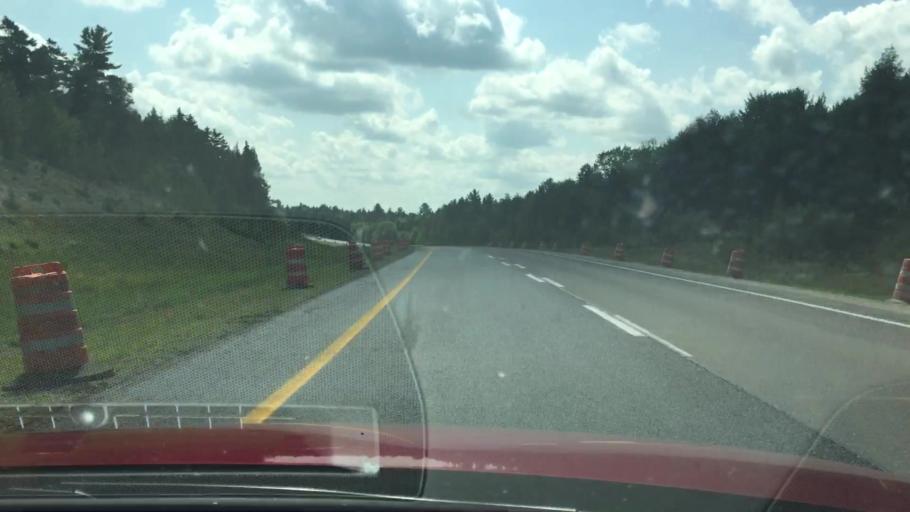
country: US
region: Maine
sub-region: Penobscot County
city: Medway
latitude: 45.6769
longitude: -68.4968
